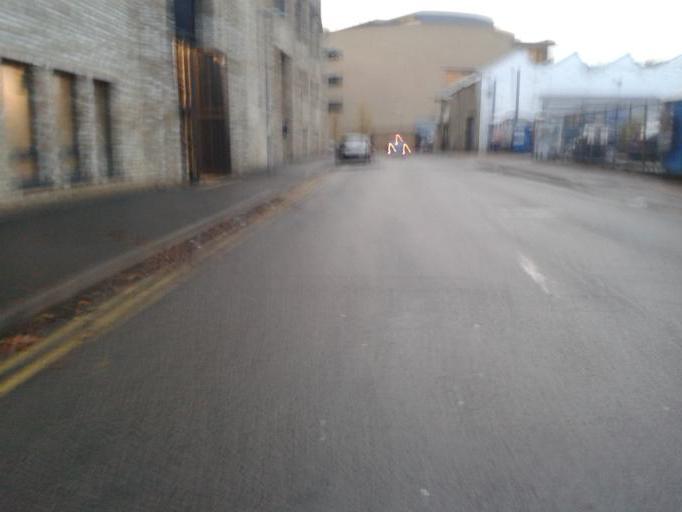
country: GB
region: England
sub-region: Cambridgeshire
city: Cambridge
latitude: 52.2072
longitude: 0.1387
